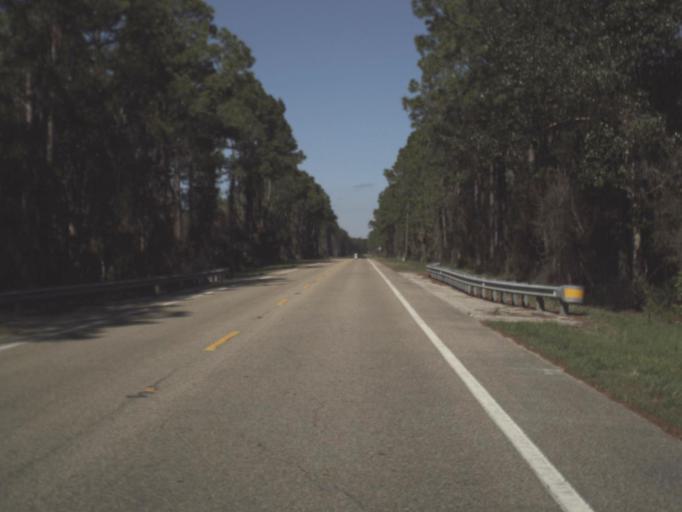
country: US
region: Florida
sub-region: Gulf County
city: Port Saint Joe
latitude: 29.8257
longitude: -85.2801
